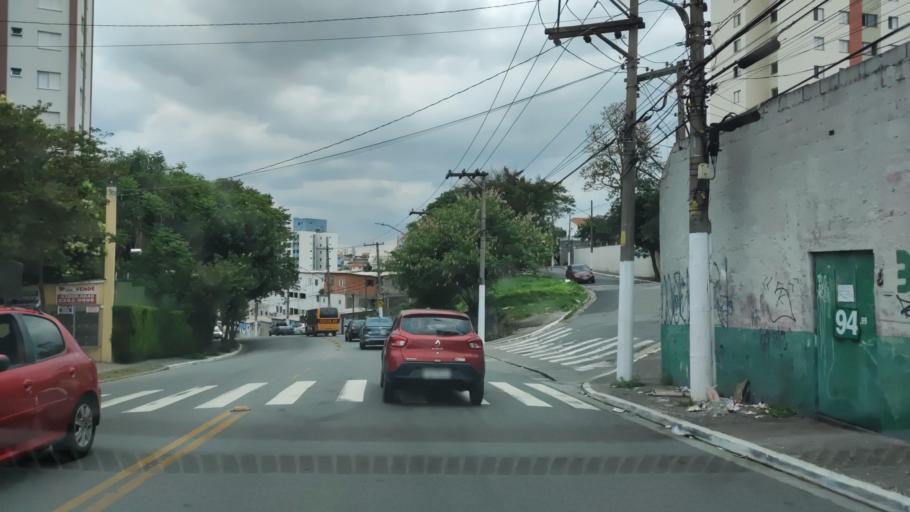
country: BR
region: Sao Paulo
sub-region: Sao Paulo
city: Sao Paulo
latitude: -23.4808
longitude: -46.6489
